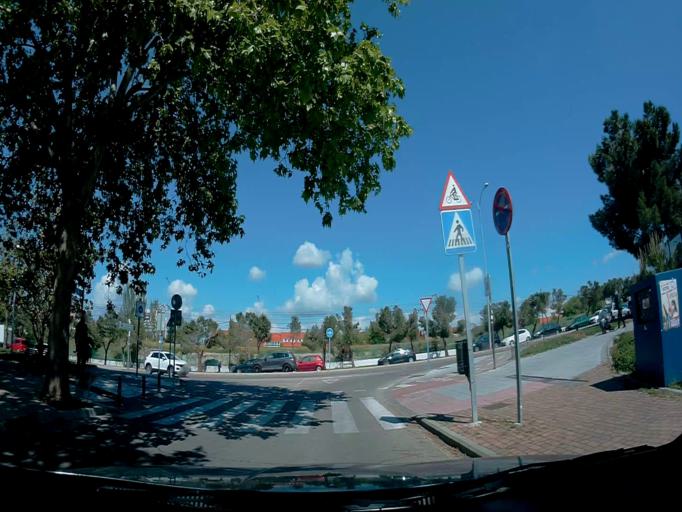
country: ES
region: Madrid
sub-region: Provincia de Madrid
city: Alcorcon
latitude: 40.3467
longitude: -3.8353
